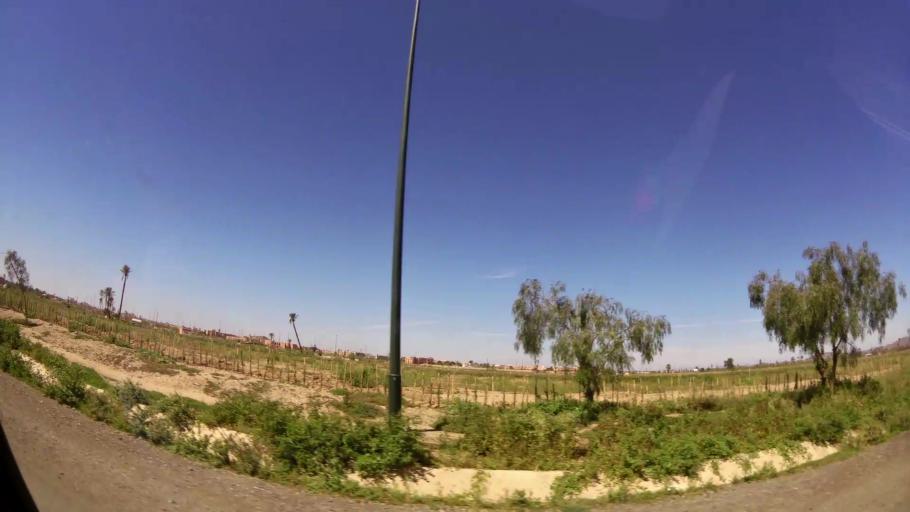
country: MA
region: Marrakech-Tensift-Al Haouz
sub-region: Marrakech
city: Marrakesh
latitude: 31.6788
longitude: -7.9914
